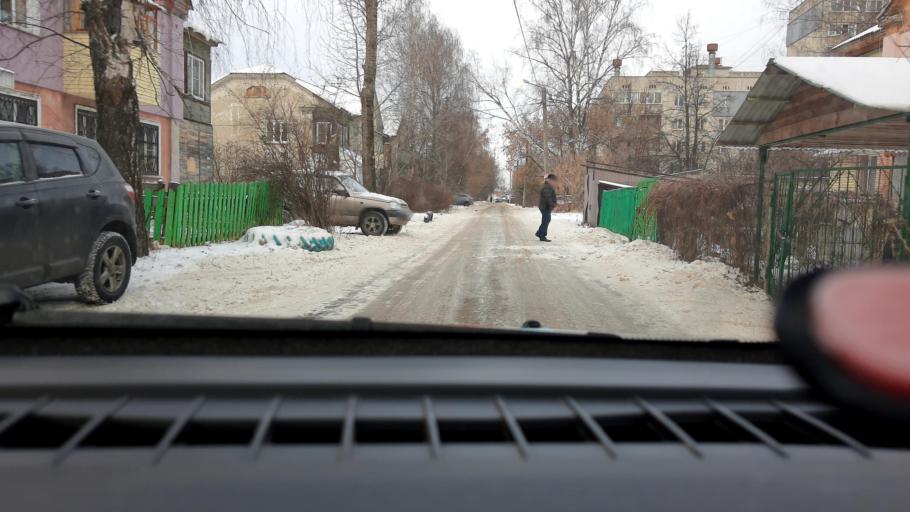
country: RU
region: Nizjnij Novgorod
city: Gorbatovka
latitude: 56.3571
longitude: 43.8462
